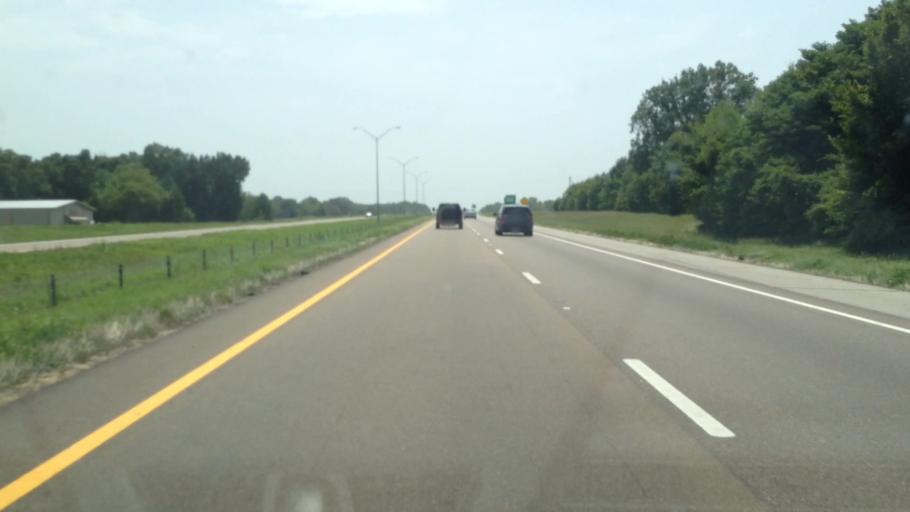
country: US
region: Texas
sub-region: Morris County
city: Omaha
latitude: 33.2479
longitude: -94.8544
